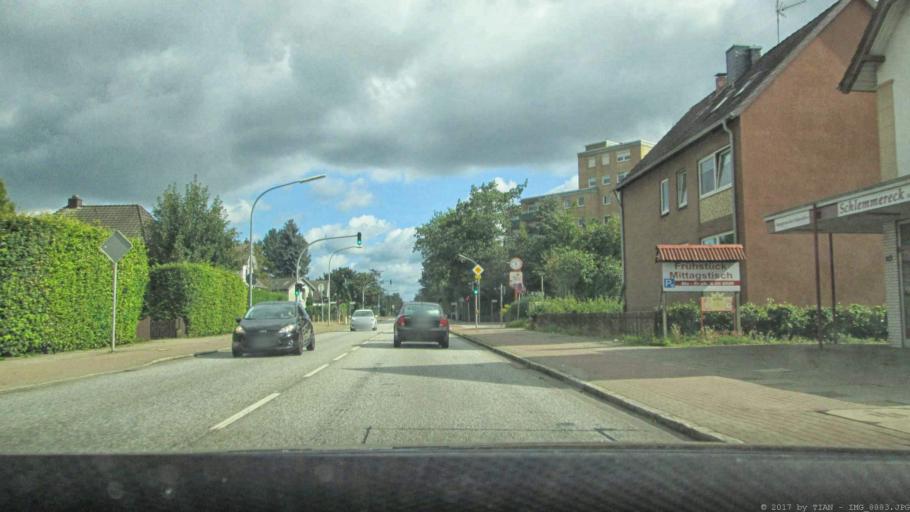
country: DE
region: Schleswig-Holstein
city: Norderstedt
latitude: 53.6749
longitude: 9.9873
